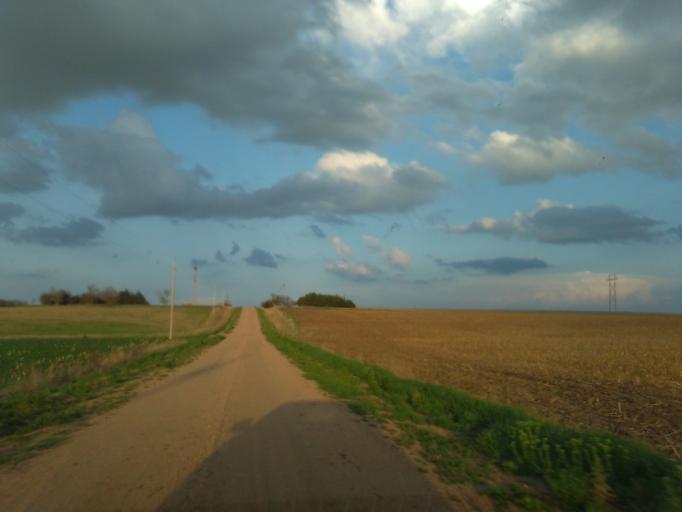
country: US
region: Nebraska
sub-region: Webster County
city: Red Cloud
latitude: 40.2199
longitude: -98.3429
